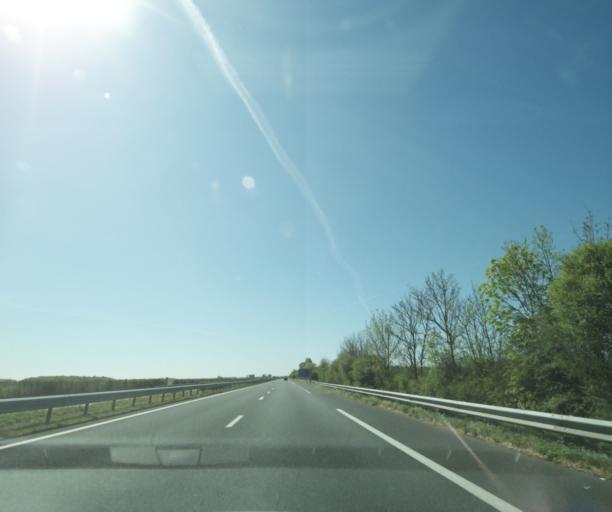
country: FR
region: Centre
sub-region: Departement de l'Indre
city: Luant
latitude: 46.6893
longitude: 1.5827
